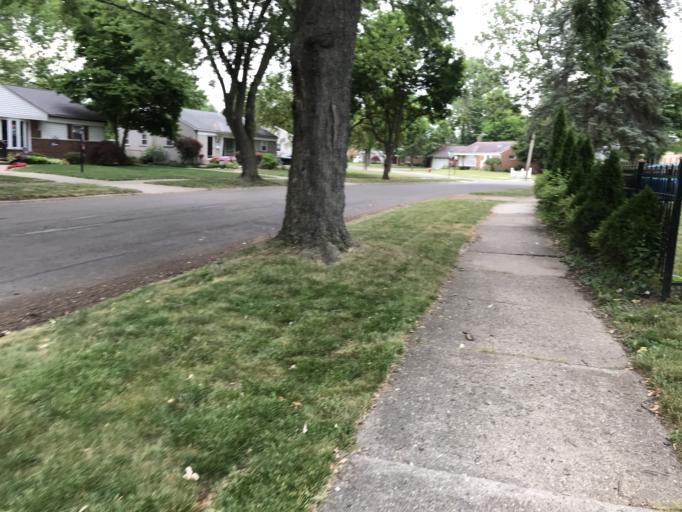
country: US
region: Michigan
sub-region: Oakland County
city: Farmington
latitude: 42.4682
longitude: -83.3597
